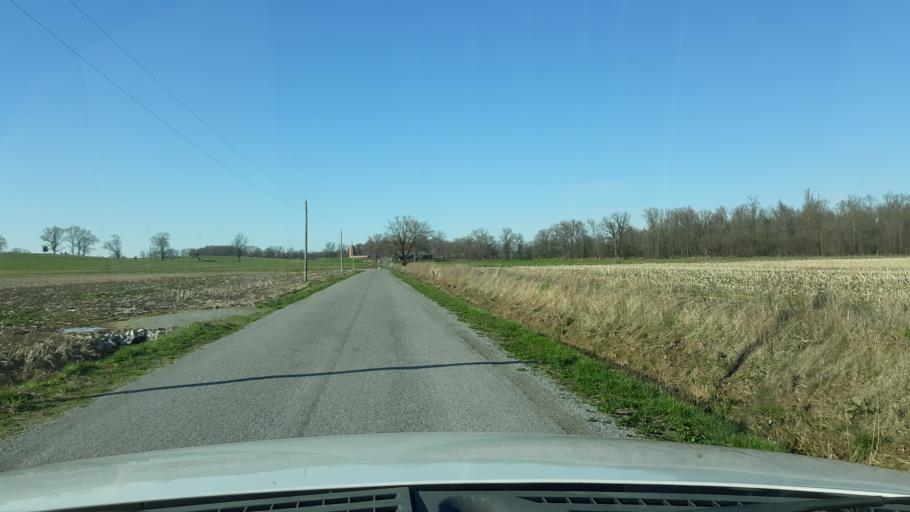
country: US
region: Illinois
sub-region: Saline County
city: Harrisburg
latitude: 37.7735
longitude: -88.5863
